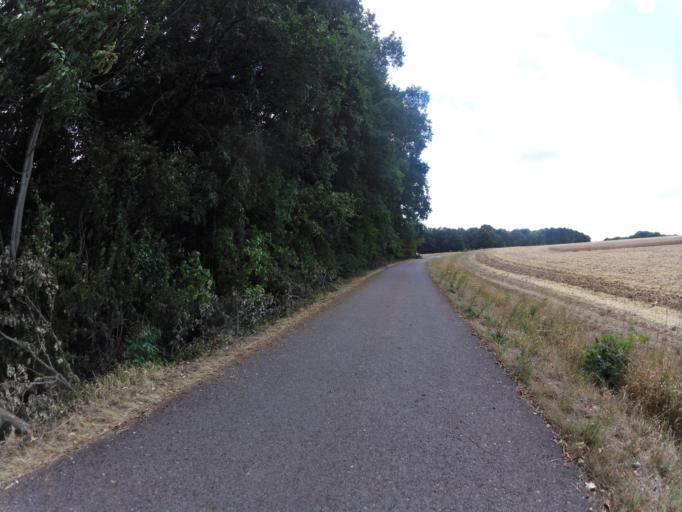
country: DE
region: Bavaria
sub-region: Regierungsbezirk Unterfranken
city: Aub
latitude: 49.5398
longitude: 10.0417
